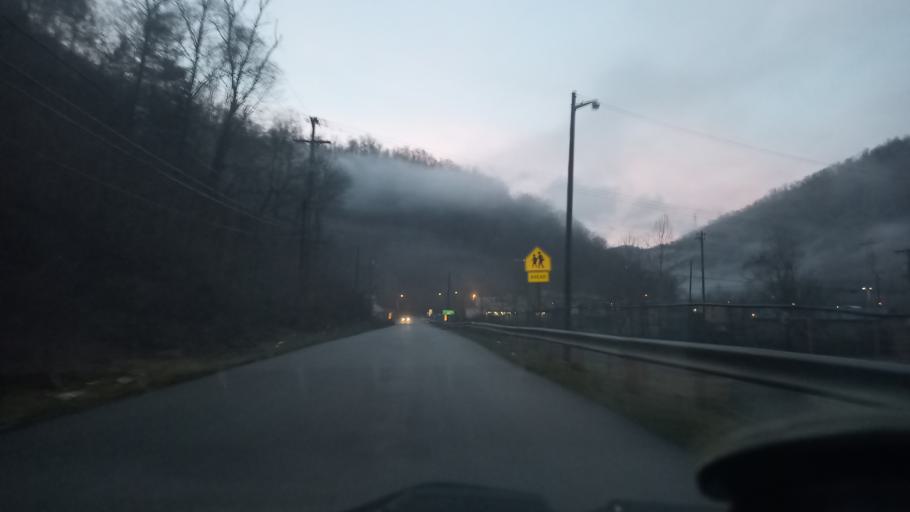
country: US
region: West Virginia
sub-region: Logan County
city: Mallory
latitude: 37.7282
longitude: -81.8775
